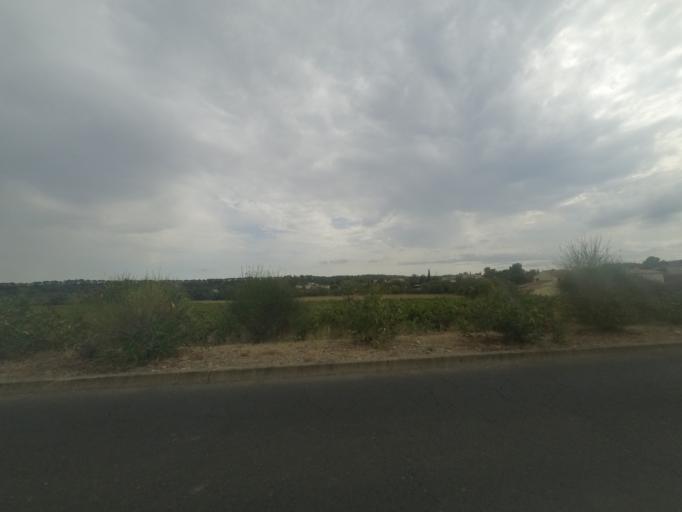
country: FR
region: Languedoc-Roussillon
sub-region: Departement de l'Herault
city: Les Matelles
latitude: 43.7318
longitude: 3.8180
